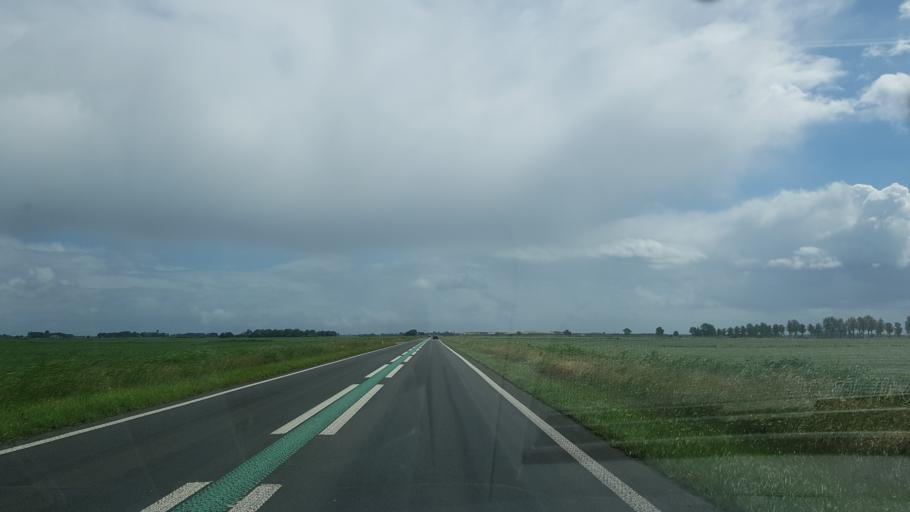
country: NL
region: Friesland
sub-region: Gemeente Ferwerderadiel
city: Burdaard
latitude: 53.2737
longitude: 5.8869
